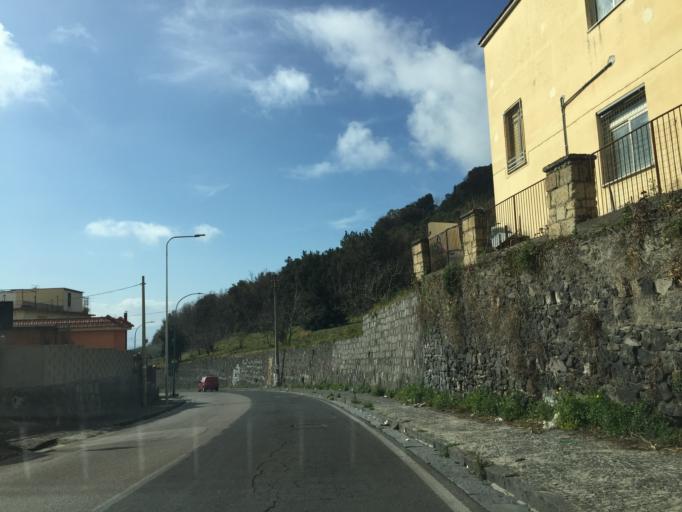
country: IT
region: Campania
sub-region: Provincia di Napoli
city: Torre del Greco
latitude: 40.7826
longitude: 14.4083
